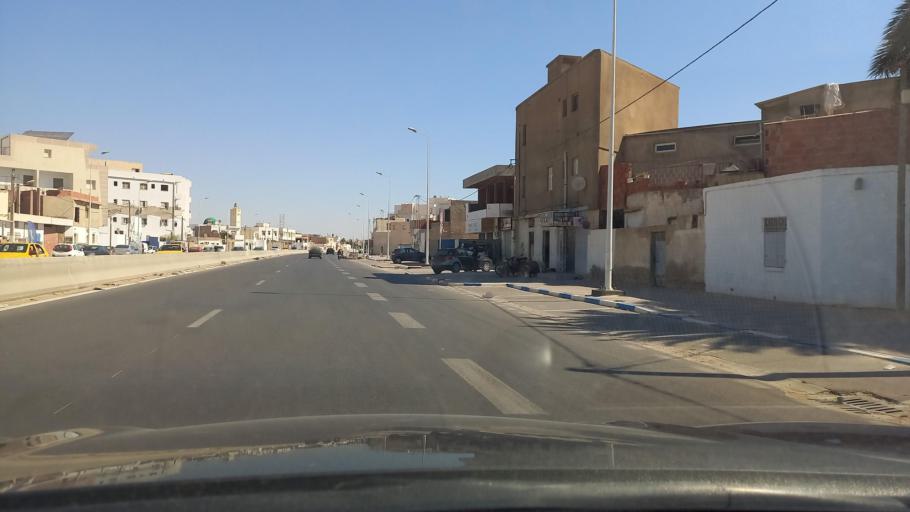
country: TN
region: Safaqis
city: Sfax
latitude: 34.7380
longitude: 10.7238
